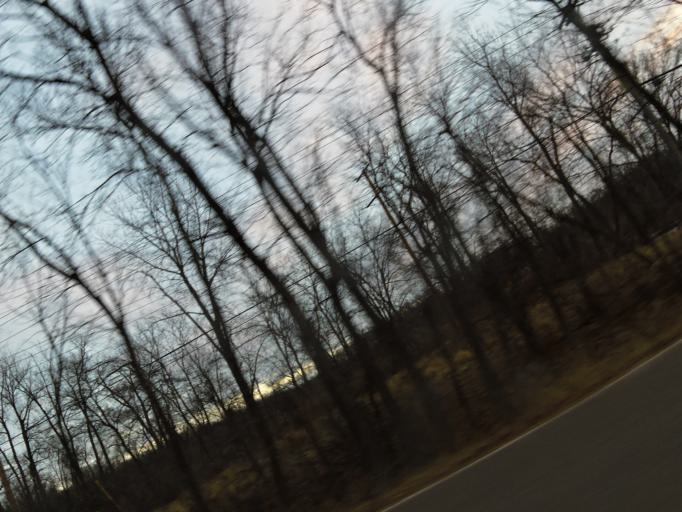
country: US
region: Minnesota
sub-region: Washington County
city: Birchwood
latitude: 45.0545
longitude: -92.9638
